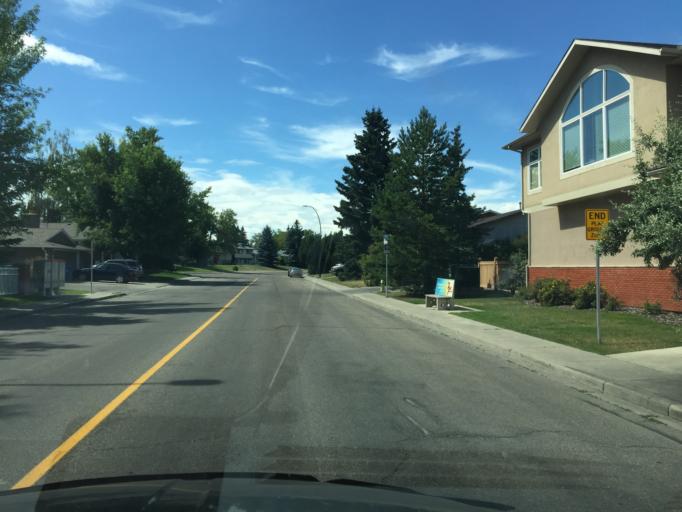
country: CA
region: Alberta
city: Calgary
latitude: 50.9416
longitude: -114.0628
